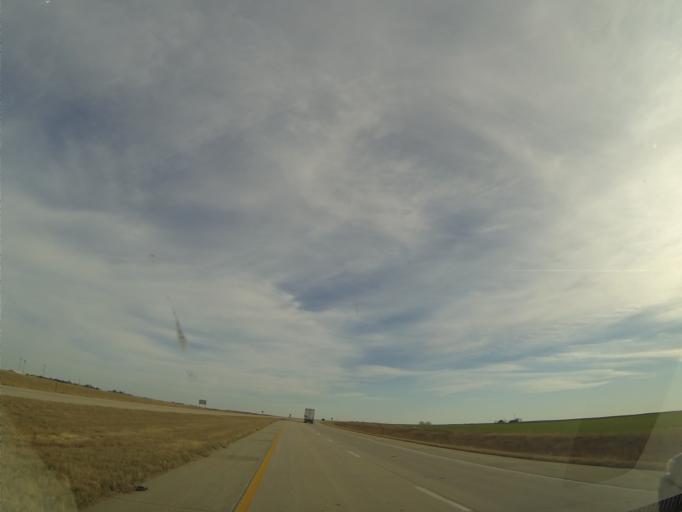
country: US
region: Kansas
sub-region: Ottawa County
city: Minneapolis
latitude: 39.1078
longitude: -97.6563
